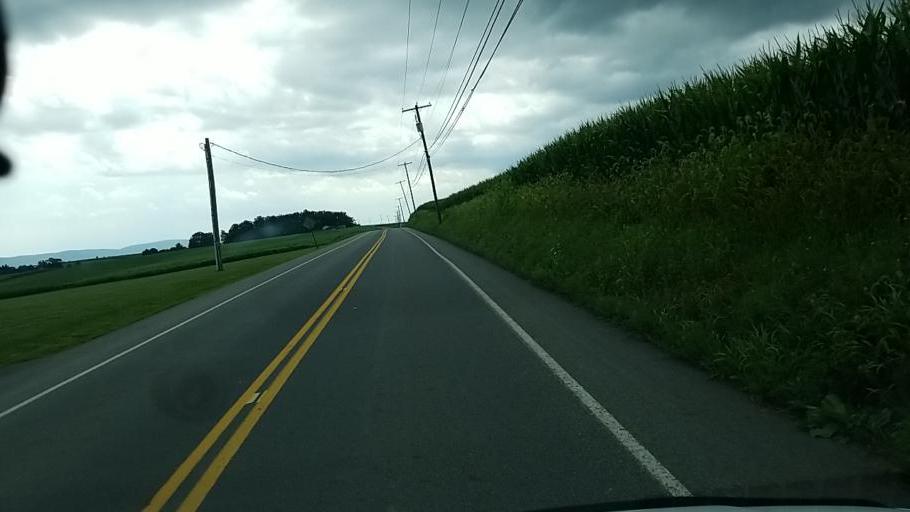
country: US
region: Pennsylvania
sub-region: Dauphin County
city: Elizabethville
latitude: 40.6002
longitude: -76.8193
